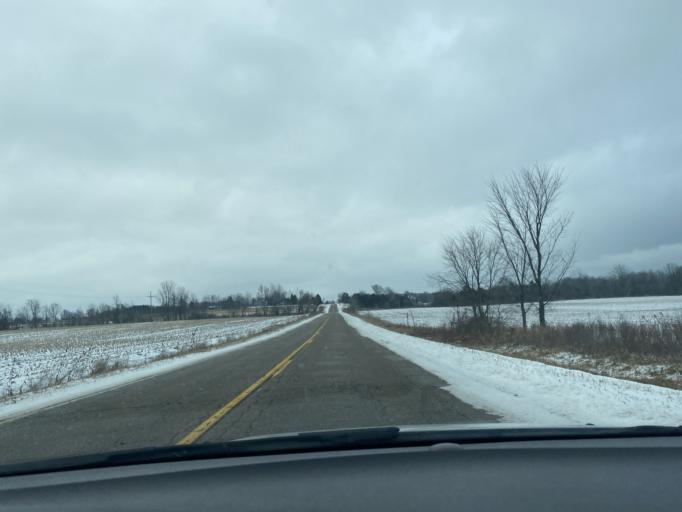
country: US
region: Michigan
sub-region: Lapeer County
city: North Branch
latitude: 43.2083
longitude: -83.1692
